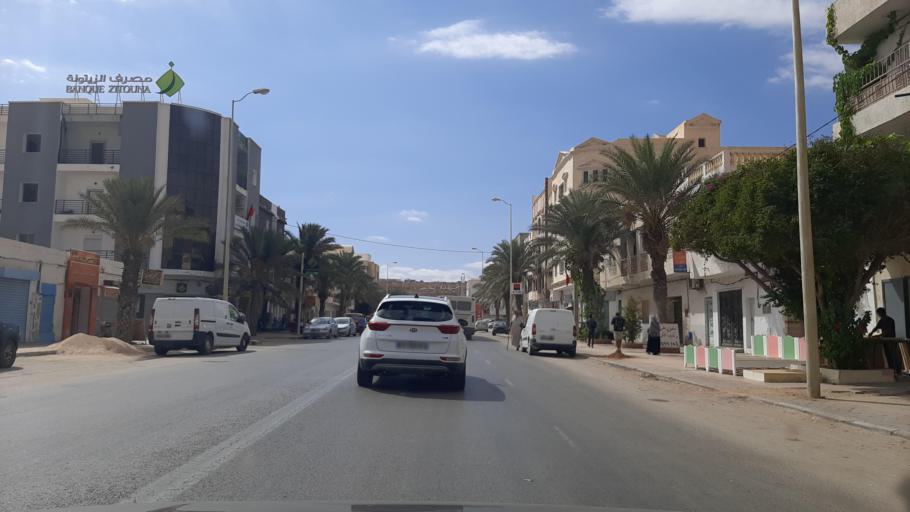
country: TN
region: Tataouine
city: Tataouine
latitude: 32.9373
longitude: 10.4517
